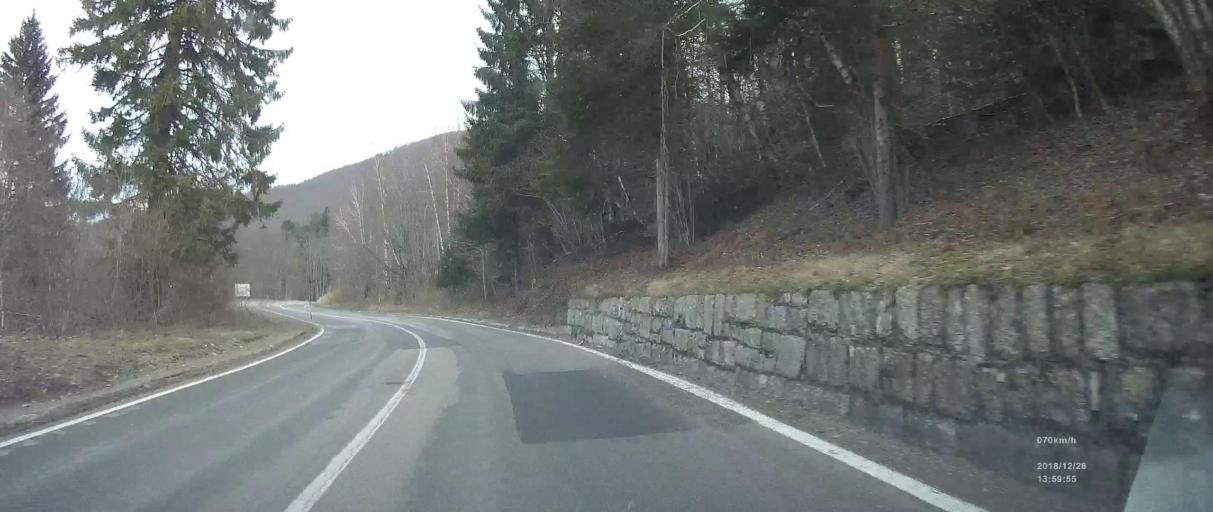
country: SI
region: Kostel
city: Kostel
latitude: 45.4067
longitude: 14.9135
